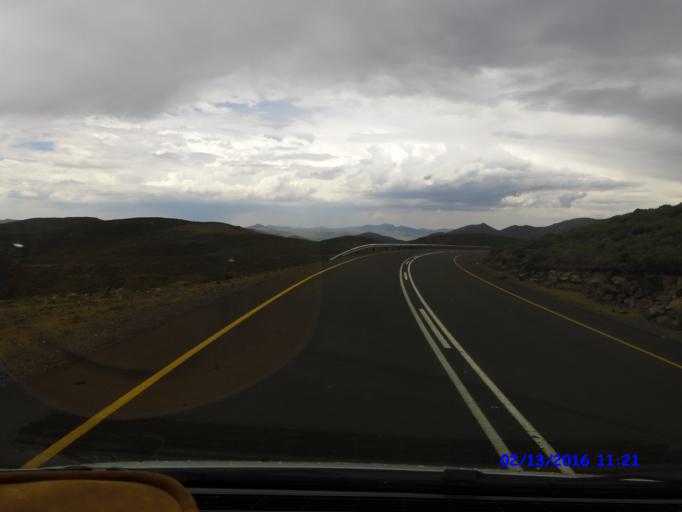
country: LS
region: Maseru
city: Nako
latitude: -29.7561
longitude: 27.9793
